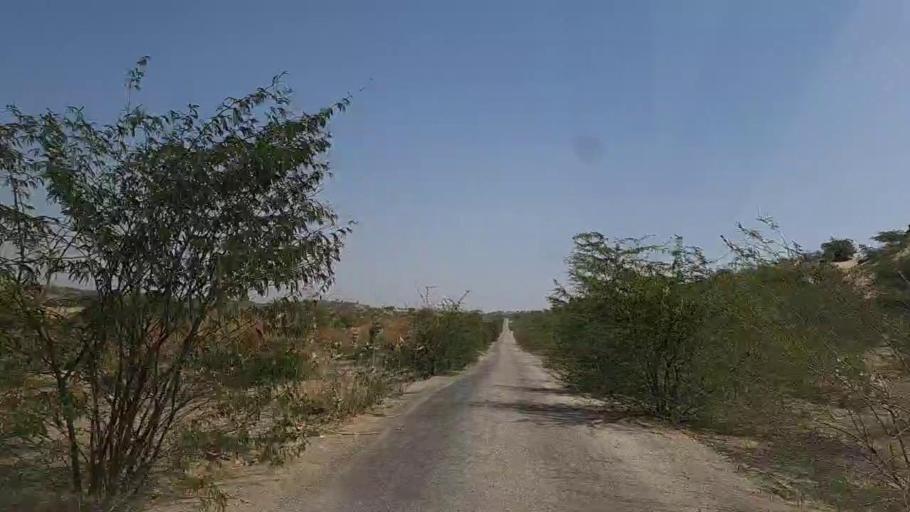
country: PK
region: Sindh
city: Diplo
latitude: 24.4851
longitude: 69.4609
